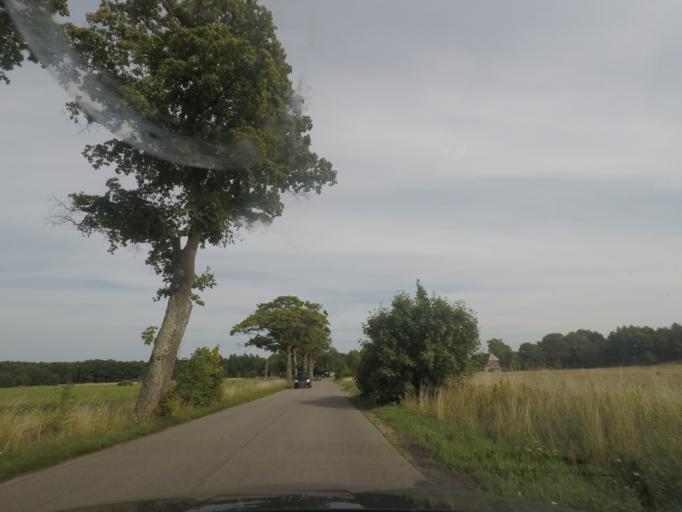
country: PL
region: Pomeranian Voivodeship
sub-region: Slupsk
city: Slupsk
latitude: 54.5963
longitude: 17.0633
